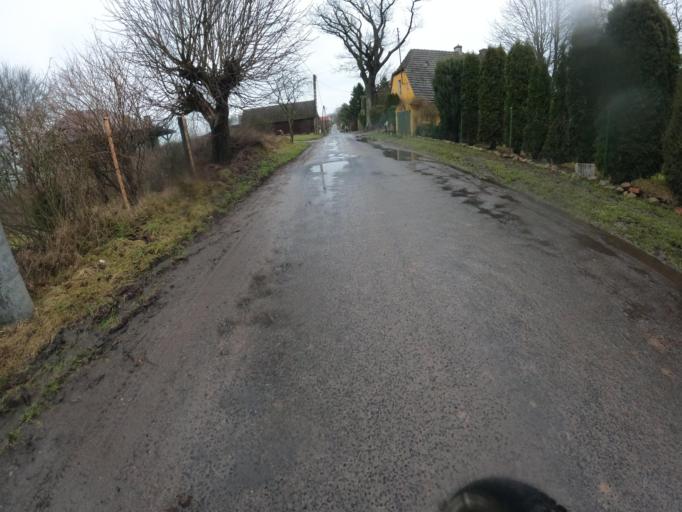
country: PL
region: West Pomeranian Voivodeship
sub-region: Powiat slawienski
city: Darlowo
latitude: 54.3944
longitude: 16.5274
